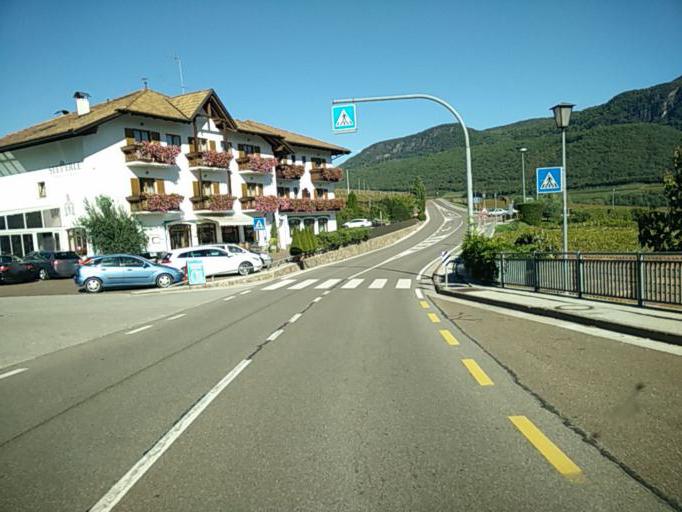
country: IT
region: Trentino-Alto Adige
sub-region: Bolzano
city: Caldaro sulla Strada del Vino
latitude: 46.3856
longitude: 11.2539
